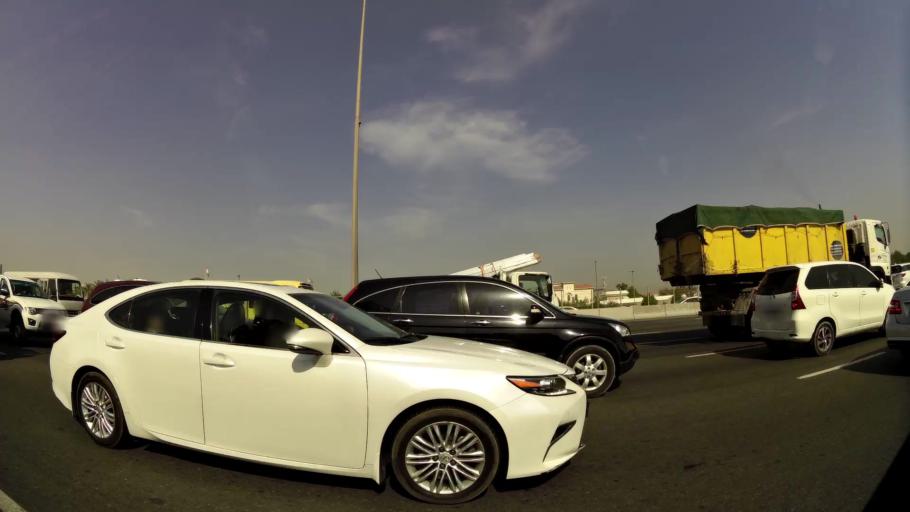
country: AE
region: Ash Shariqah
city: Sharjah
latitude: 25.2445
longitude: 55.4050
